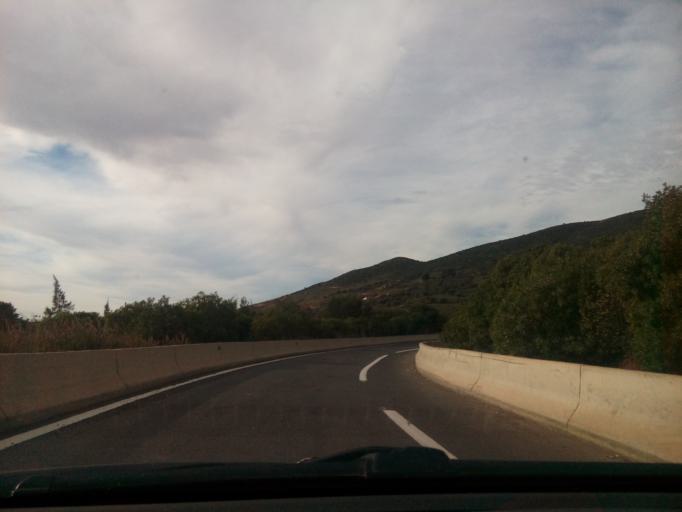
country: DZ
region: Sidi Bel Abbes
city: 'Ain el Berd
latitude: 35.3829
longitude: -0.5000
